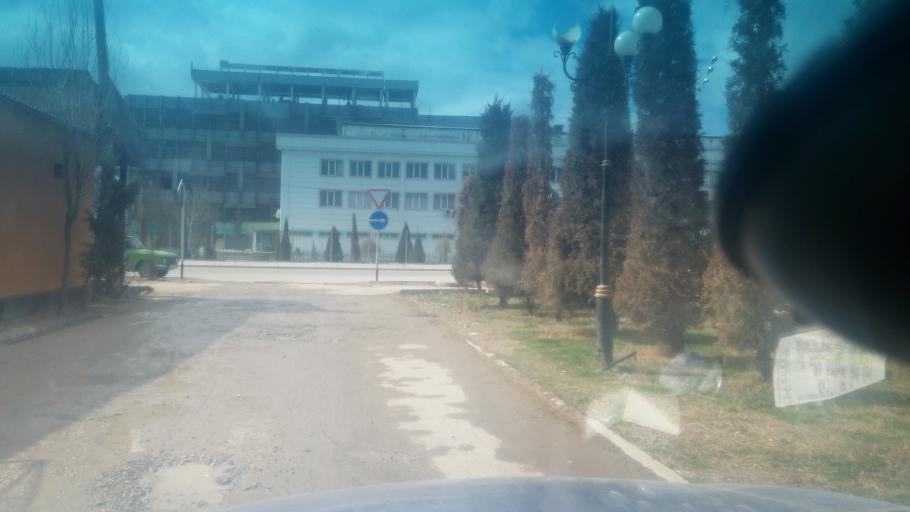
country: UZ
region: Sirdaryo
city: Guliston
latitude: 40.5181
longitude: 68.7692
